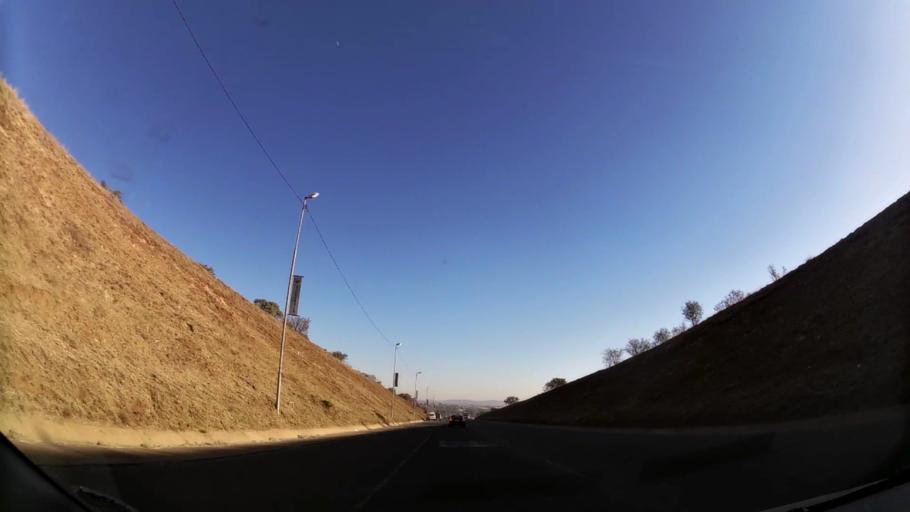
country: ZA
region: Gauteng
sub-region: West Rand District Municipality
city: Muldersdriseloop
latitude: -26.0710
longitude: 27.8518
